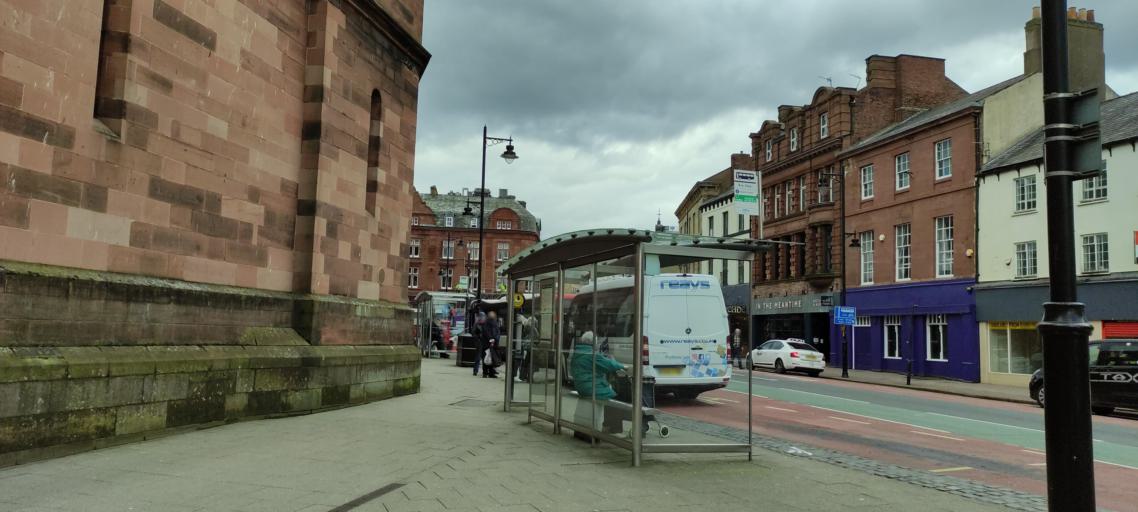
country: GB
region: England
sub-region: Cumbria
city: Carlisle
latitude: 54.8921
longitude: -2.9337
